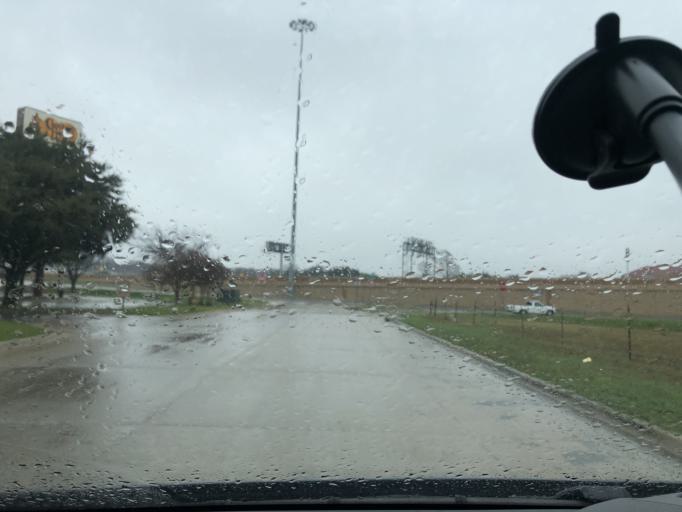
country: US
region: Texas
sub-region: Tarrant County
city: Blue Mound
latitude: 32.8266
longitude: -97.3141
